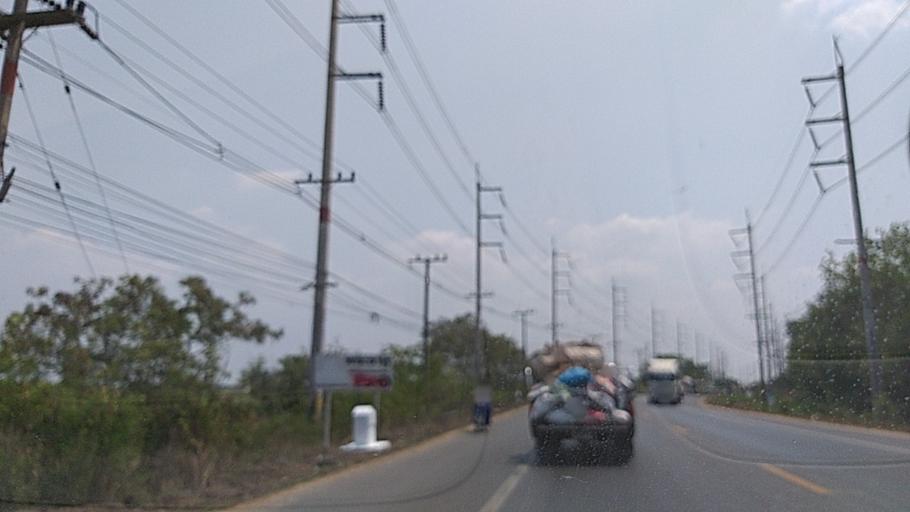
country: TH
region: Chachoengsao
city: Bang Nam Priao
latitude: 13.7796
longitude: 101.0619
